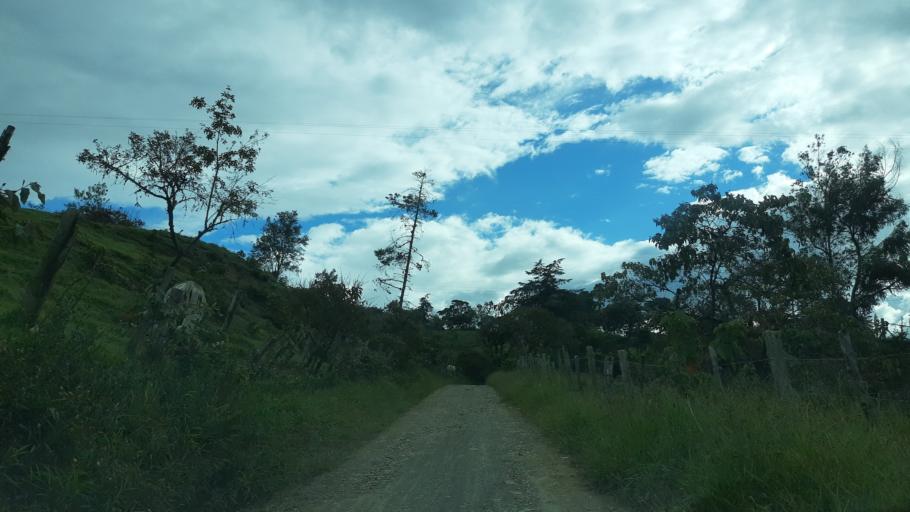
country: CO
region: Boyaca
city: Garagoa
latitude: 5.0139
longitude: -73.3373
